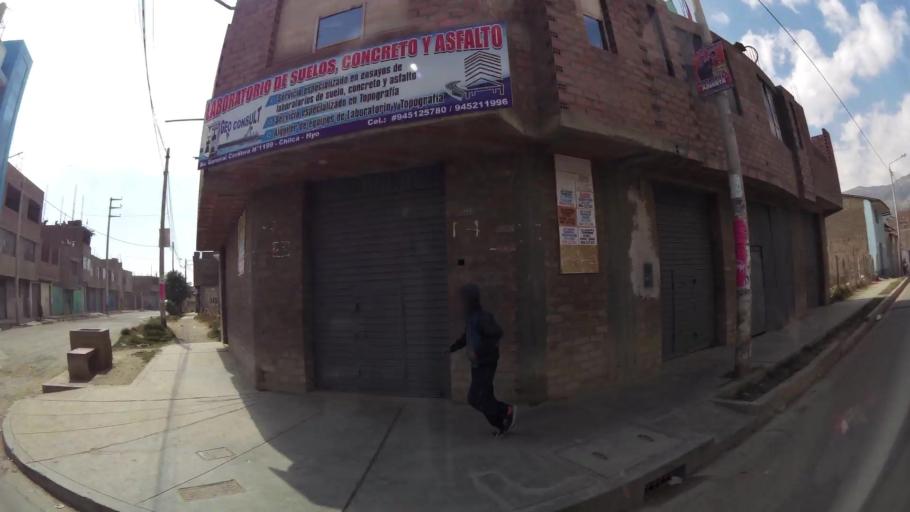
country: PE
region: Junin
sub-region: Provincia de Huancayo
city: Huancayo
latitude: -12.0940
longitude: -75.2059
